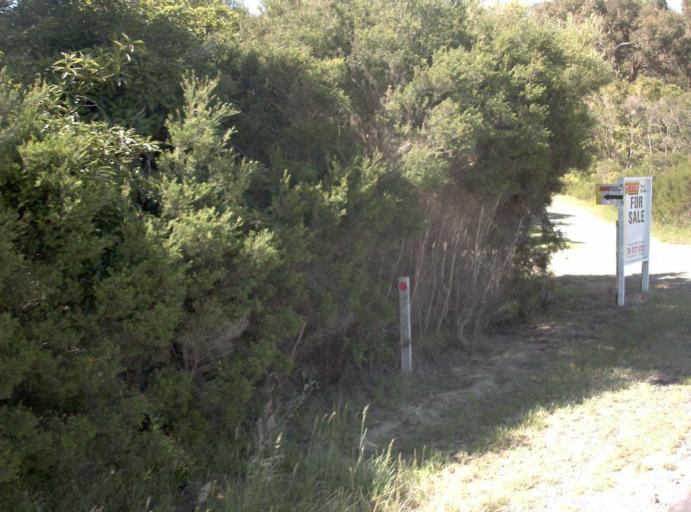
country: AU
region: Victoria
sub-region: Latrobe
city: Morwell
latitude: -38.6640
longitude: 146.4090
